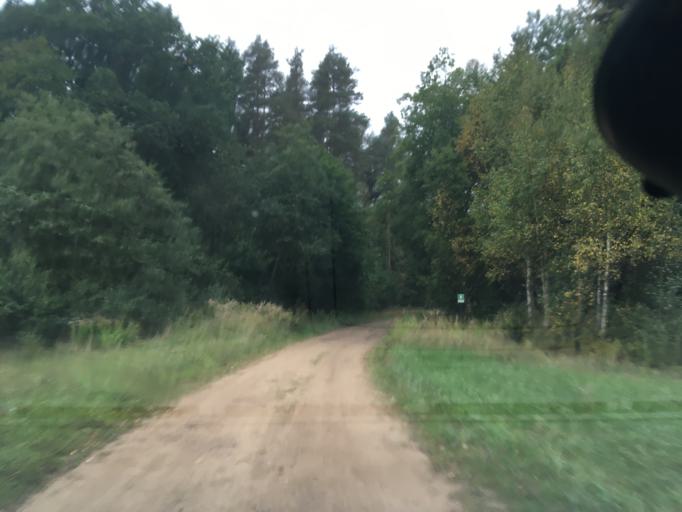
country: LV
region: Kuldigas Rajons
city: Kuldiga
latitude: 56.9867
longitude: 22.0127
